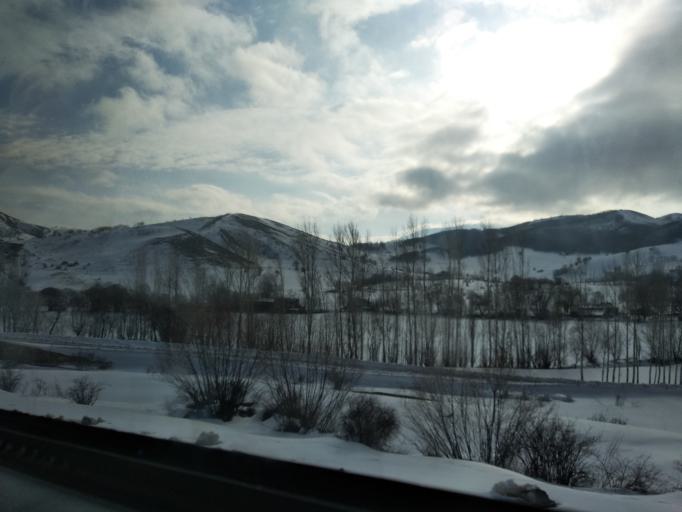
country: TR
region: Erzincan
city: Catalarmut
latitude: 39.9072
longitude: 39.4035
